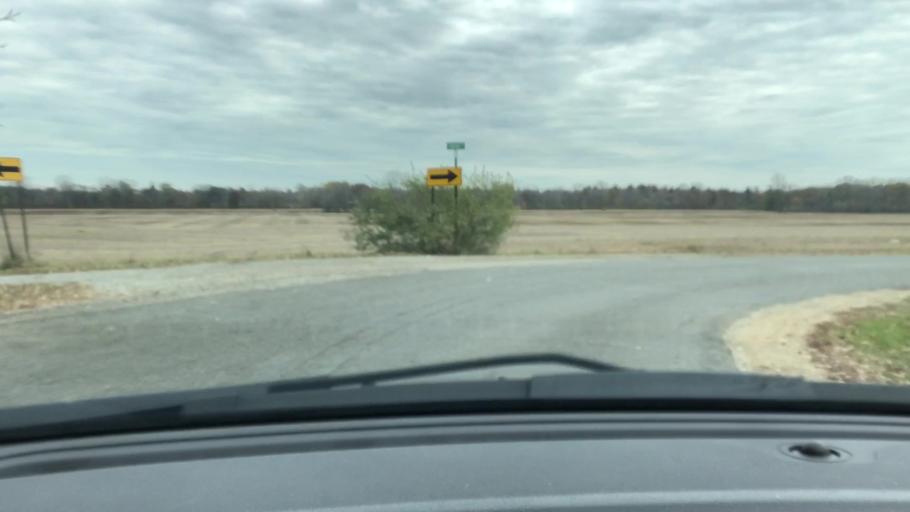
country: US
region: Michigan
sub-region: Midland County
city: Midland
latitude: 43.6412
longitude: -84.3304
